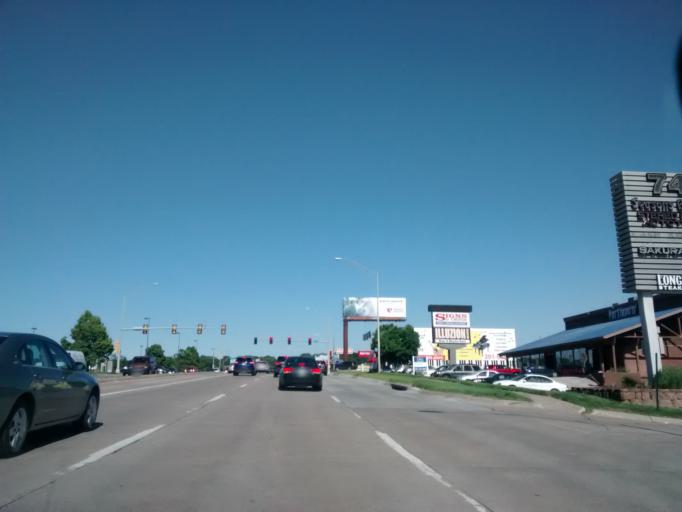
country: US
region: Nebraska
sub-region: Douglas County
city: Ralston
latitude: 41.2596
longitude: -96.0282
